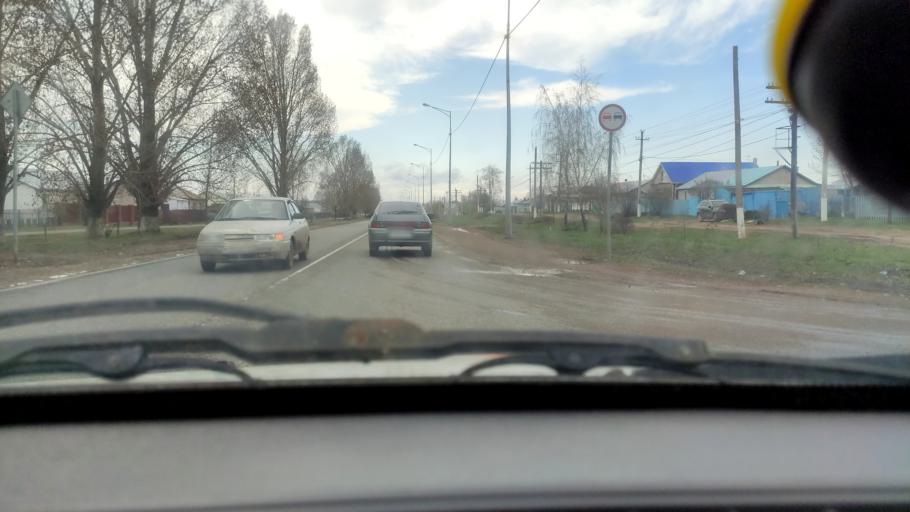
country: RU
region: Samara
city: Zhigulevsk
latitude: 53.5546
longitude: 49.5321
